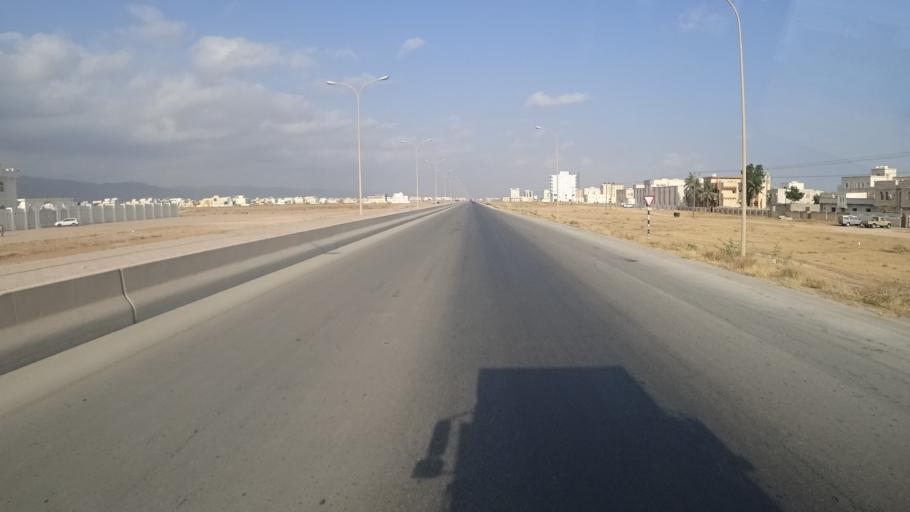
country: OM
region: Zufar
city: Salalah
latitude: 17.0236
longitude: 54.0184
